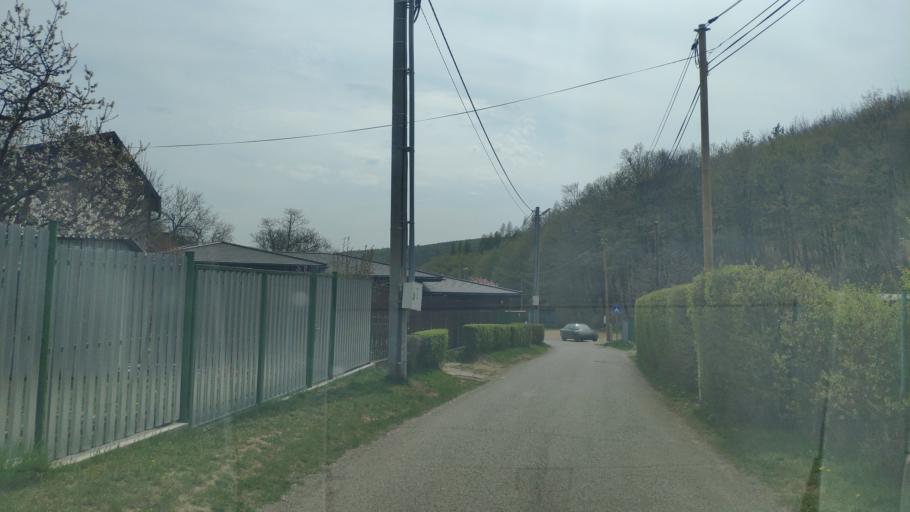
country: SK
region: Kosicky
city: Kosice
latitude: 48.7180
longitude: 21.1964
